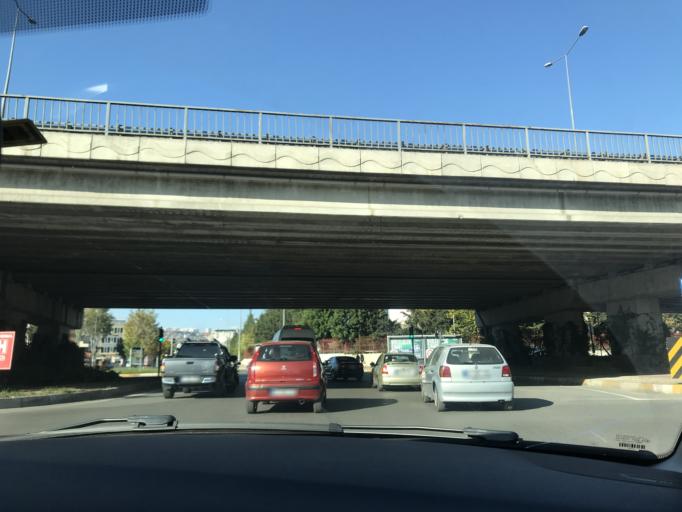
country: TR
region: Antalya
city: Antalya
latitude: 36.9106
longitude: 30.6983
